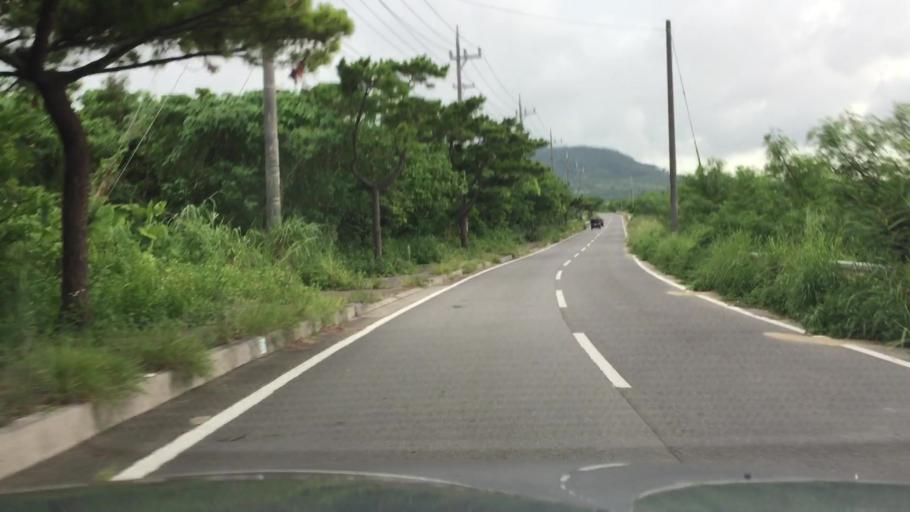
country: JP
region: Okinawa
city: Ishigaki
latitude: 24.3899
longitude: 124.1546
